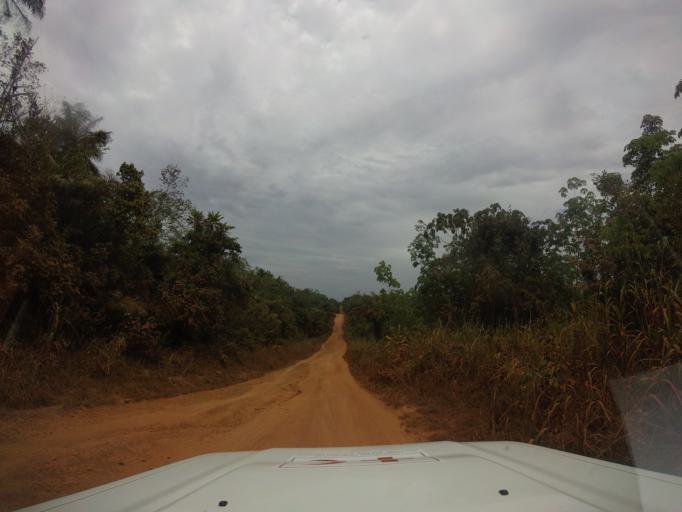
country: LR
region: Grand Cape Mount
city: Robertsport
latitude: 6.9556
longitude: -11.3209
